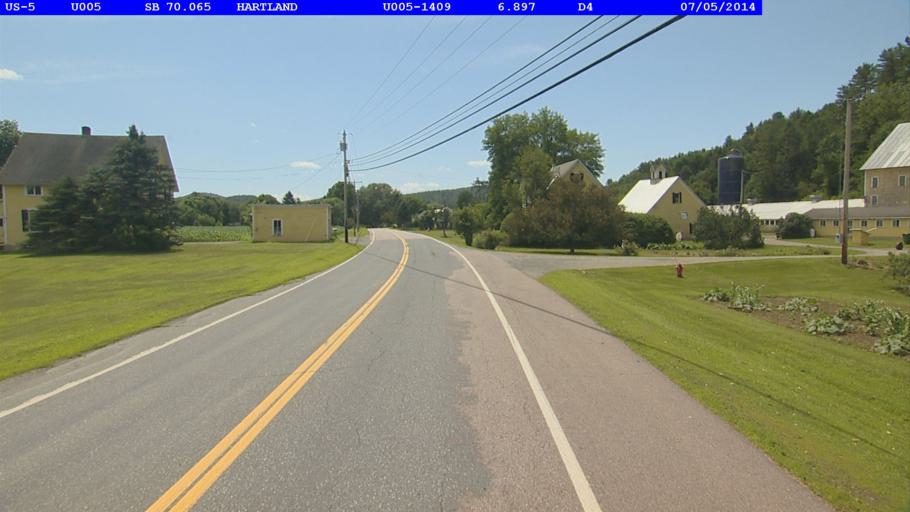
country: US
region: Vermont
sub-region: Windsor County
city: White River Junction
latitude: 43.6000
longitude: -72.3537
